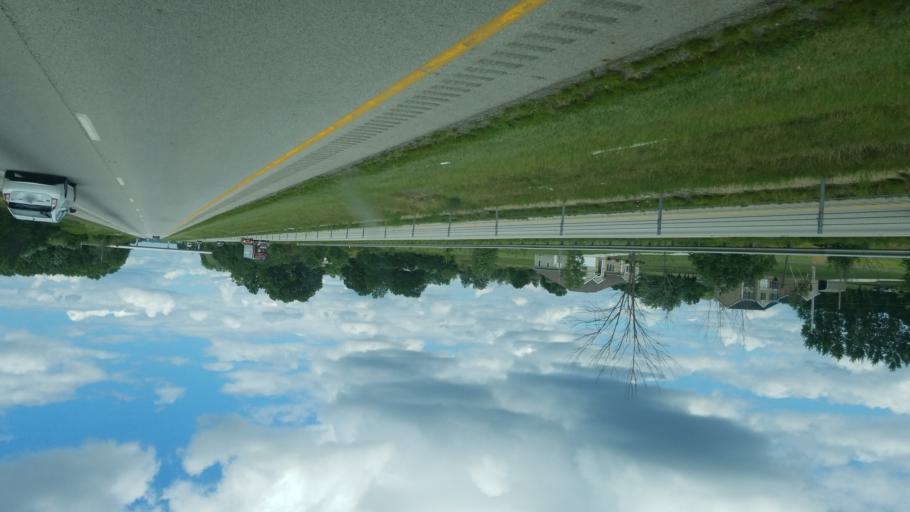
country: US
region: Ohio
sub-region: Medina County
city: Seville
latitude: 41.0319
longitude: -81.8160
